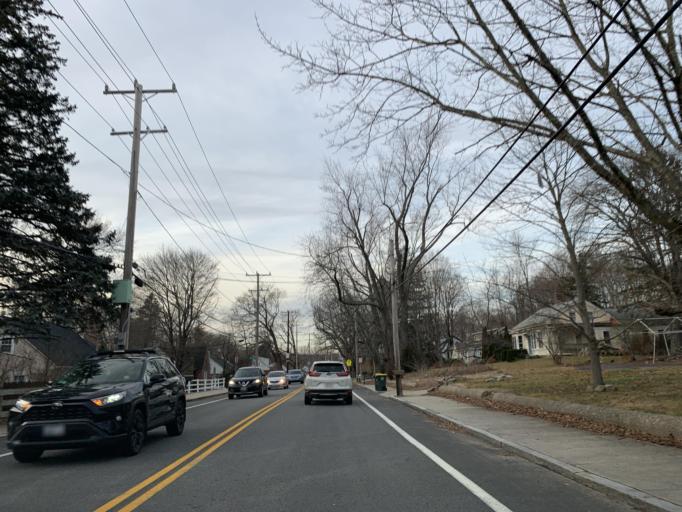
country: US
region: Rhode Island
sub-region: Providence County
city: Greenville
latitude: 41.8673
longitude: -71.5485
